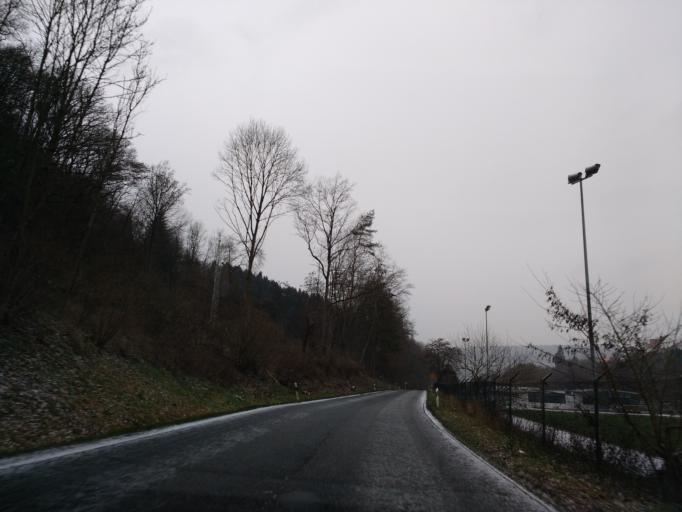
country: DE
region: Hesse
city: Spangenberg
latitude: 51.1129
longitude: 9.6744
